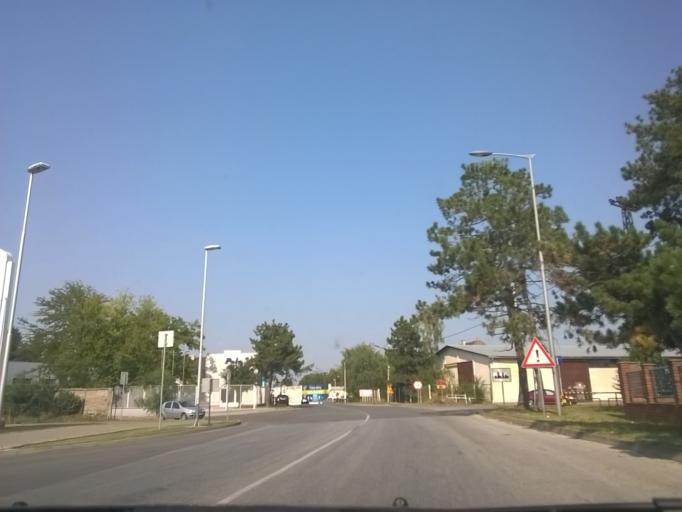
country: RS
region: Autonomna Pokrajina Vojvodina
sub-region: Juznobanatski Okrug
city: Vrsac
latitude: 45.1067
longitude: 21.2807
